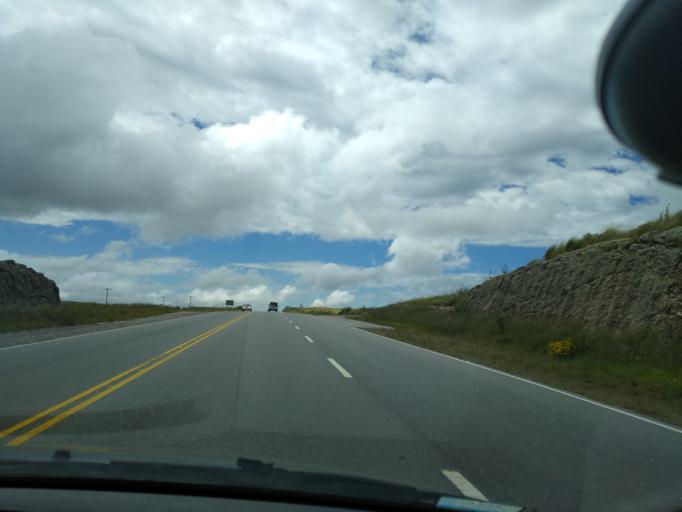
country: AR
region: Cordoba
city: Mina Clavero
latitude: -31.6105
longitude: -64.8277
